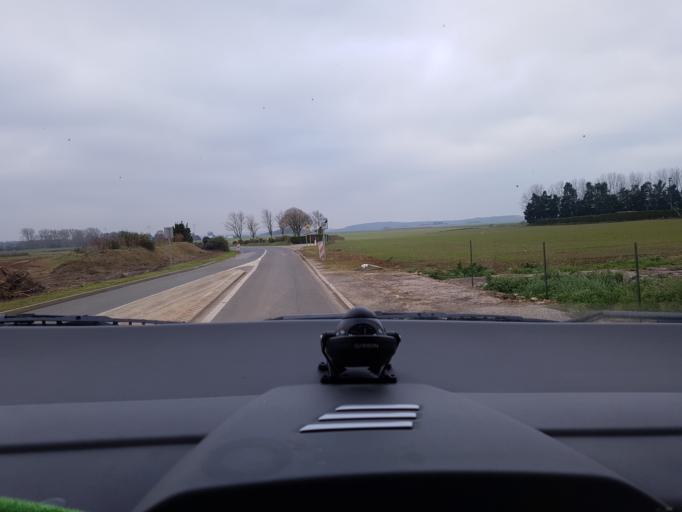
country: FR
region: Haute-Normandie
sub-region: Departement de la Seine-Maritime
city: Le Treport
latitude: 50.0363
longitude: 1.3622
